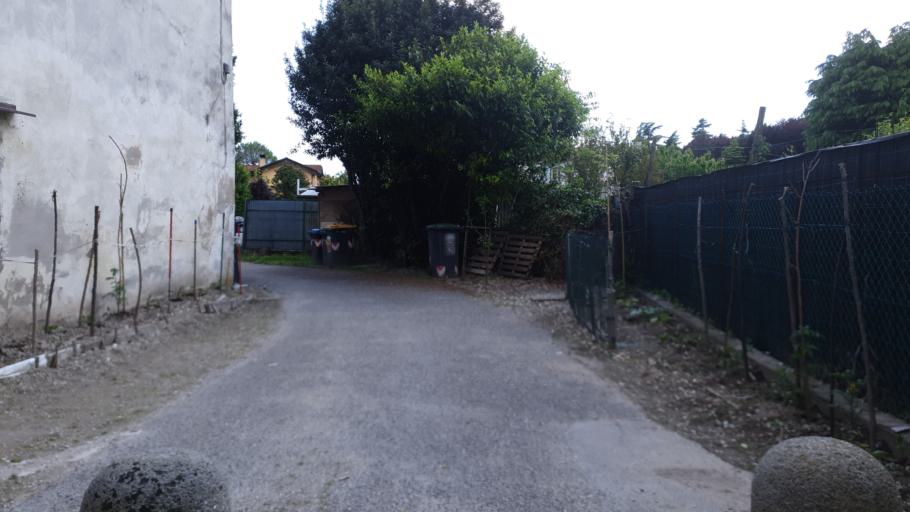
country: IT
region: Veneto
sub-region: Provincia di Padova
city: Noventa
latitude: 45.4240
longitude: 11.9495
